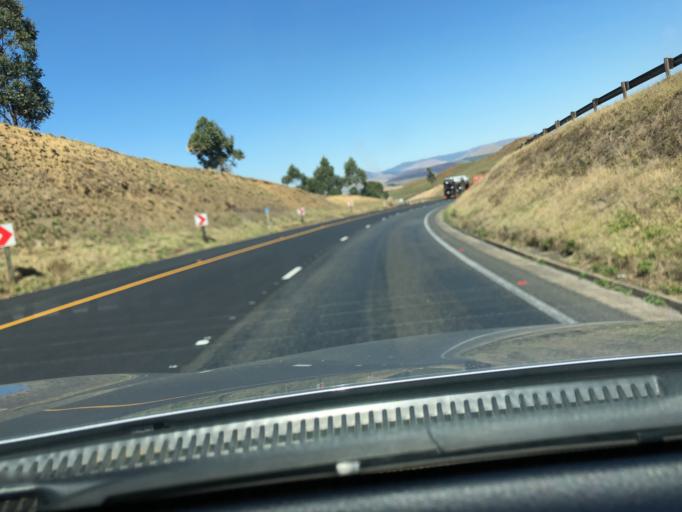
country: ZA
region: KwaZulu-Natal
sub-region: uMgungundlovu District Municipality
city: Howick
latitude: -29.4544
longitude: 30.1797
